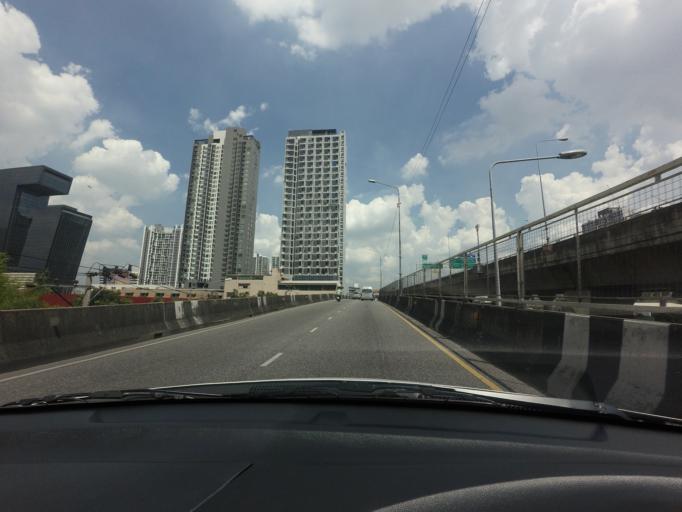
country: TH
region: Bangkok
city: Din Daeng
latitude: 13.7538
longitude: 100.5625
